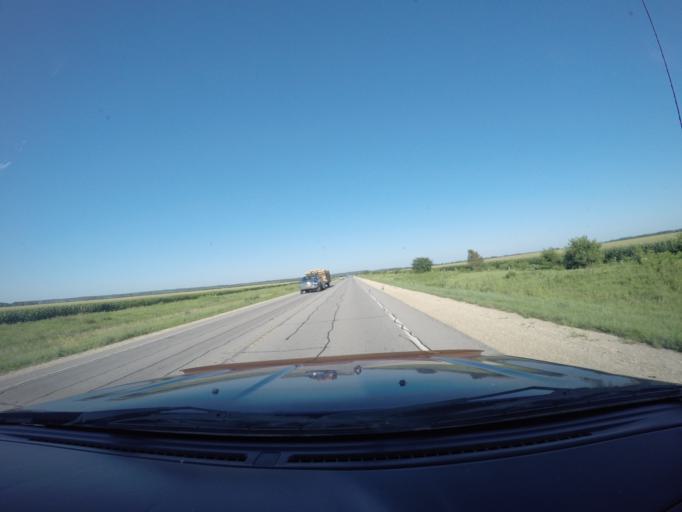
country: US
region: Kansas
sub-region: Jefferson County
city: Oskaloosa
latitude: 39.0872
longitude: -95.4461
